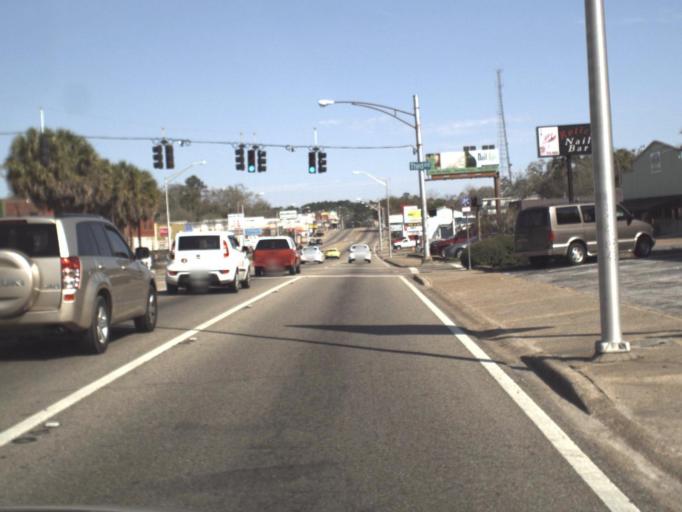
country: US
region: Florida
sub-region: Leon County
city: Tallahassee
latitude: 30.4521
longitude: -84.2807
